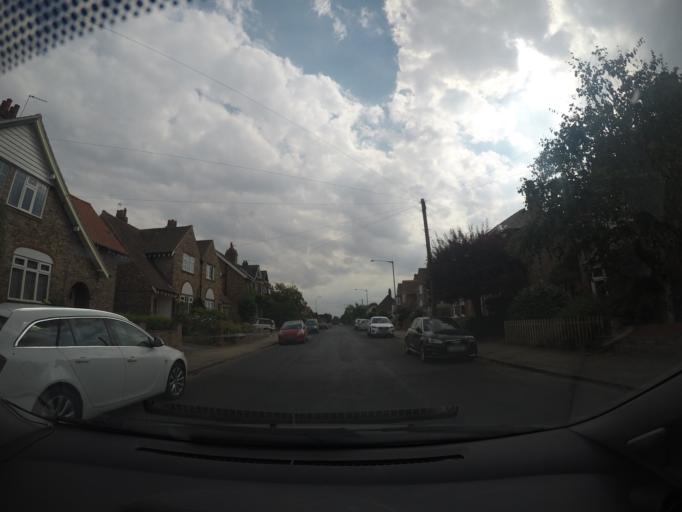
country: GB
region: England
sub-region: City of York
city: York
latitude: 53.9546
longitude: -1.1176
